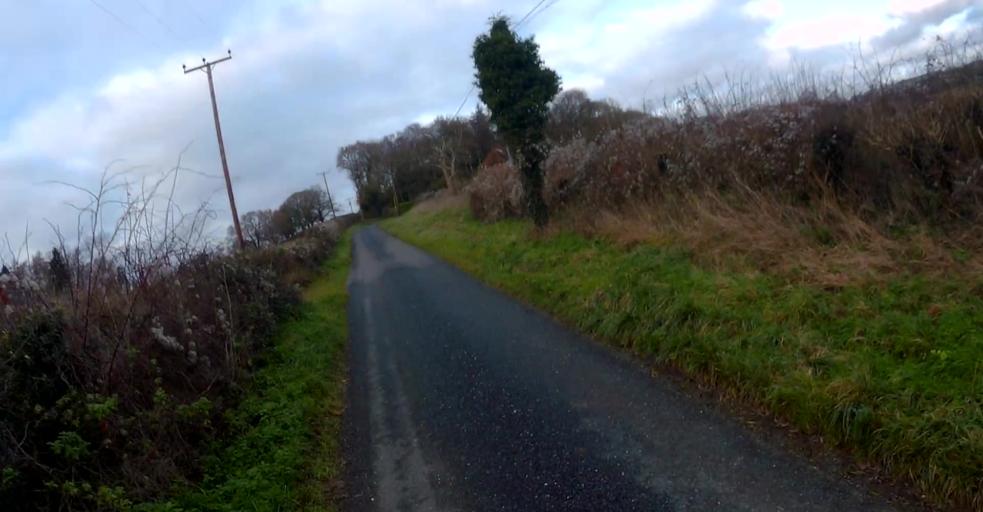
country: GB
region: England
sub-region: Hampshire
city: Four Marks
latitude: 51.1776
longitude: -1.0985
